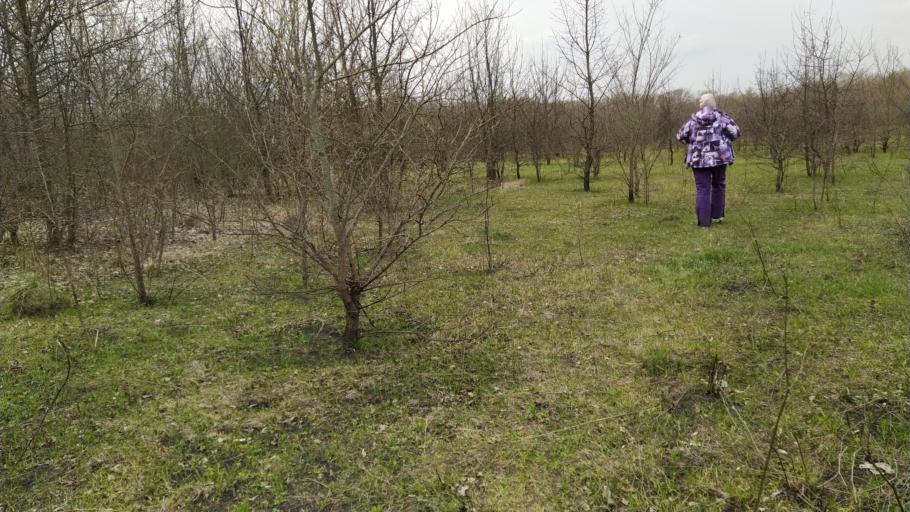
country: RU
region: Rostov
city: Semikarakorsk
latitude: 47.5406
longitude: 40.6821
